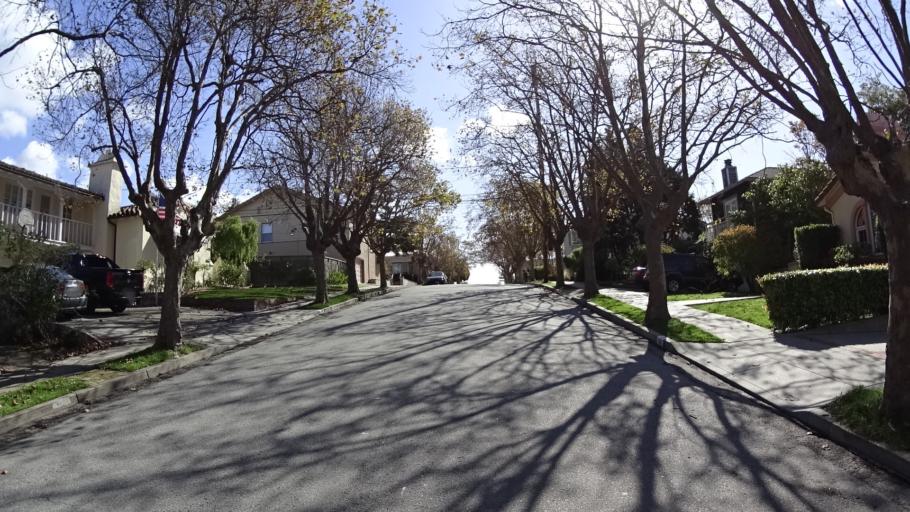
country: US
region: California
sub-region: San Mateo County
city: Millbrae
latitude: 37.5965
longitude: -122.3984
